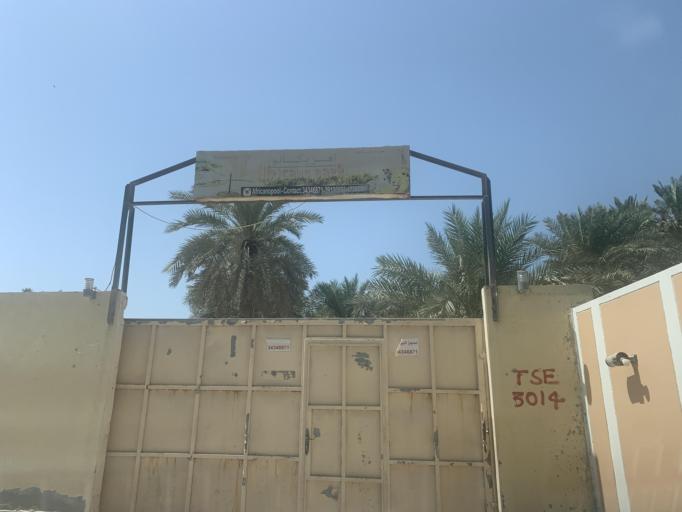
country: BH
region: Manama
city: Jidd Hafs
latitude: 26.2322
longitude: 50.5130
